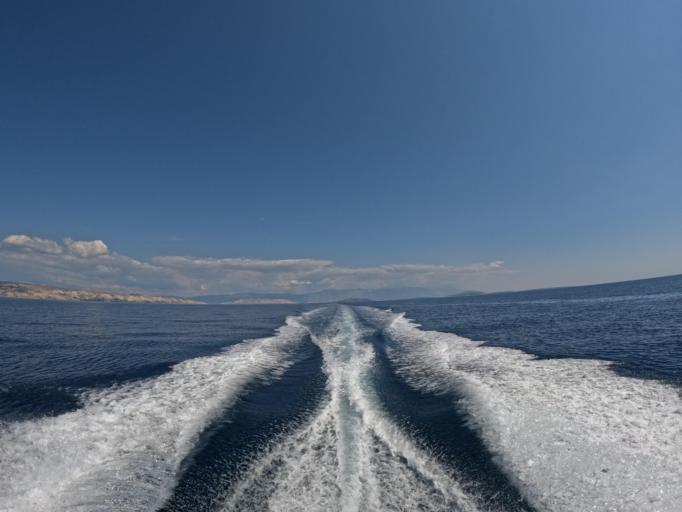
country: HR
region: Primorsko-Goranska
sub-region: Grad Krk
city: Krk
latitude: 44.9218
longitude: 14.5580
